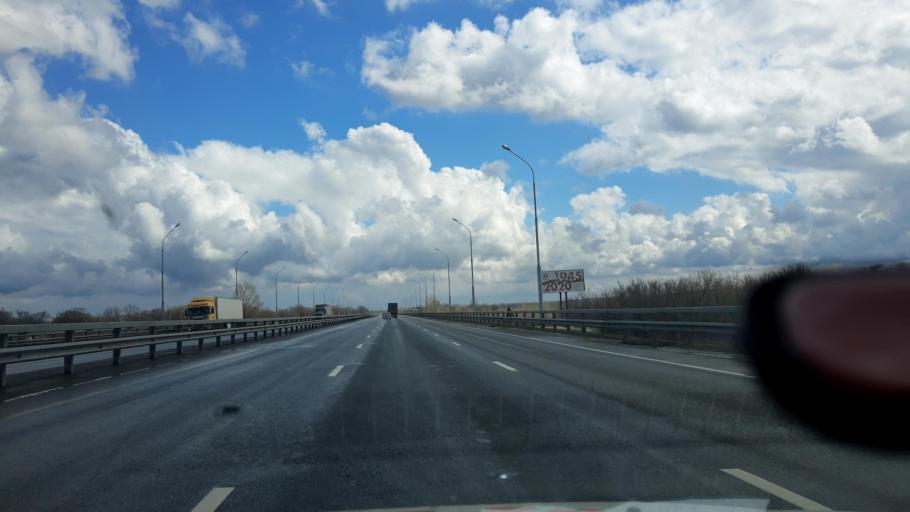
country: RU
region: Bashkortostan
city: Ufa
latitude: 54.6426
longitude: 55.9638
